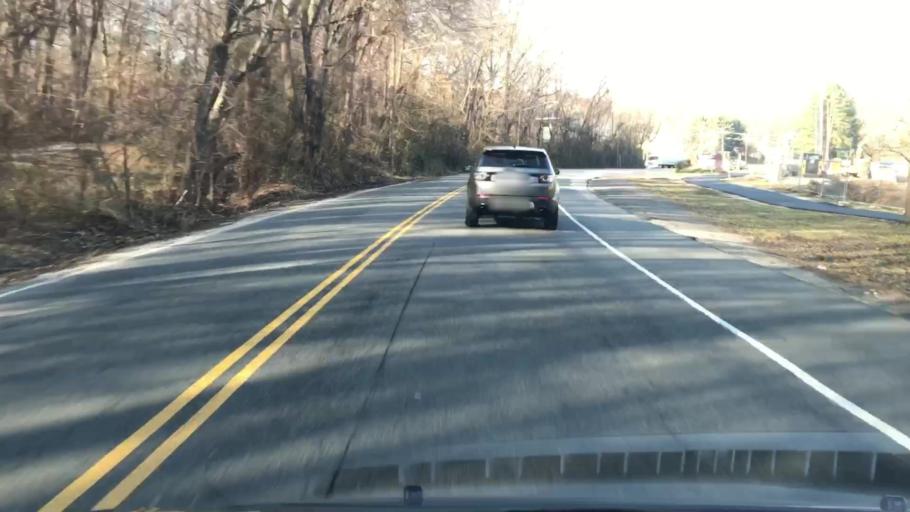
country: US
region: Virginia
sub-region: Fairfax County
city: Belle Haven
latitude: 38.7714
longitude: -77.0619
